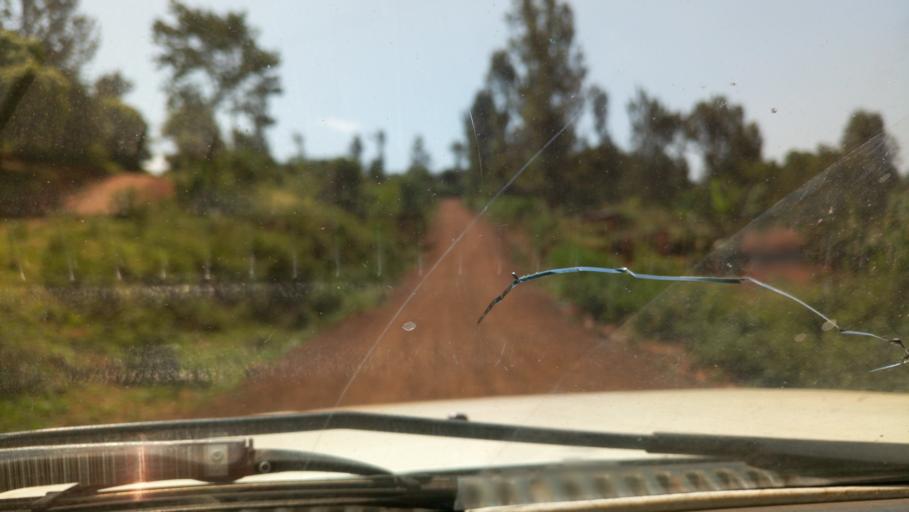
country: KE
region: Murang'a District
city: Murang'a
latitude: -0.6679
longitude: 37.1340
